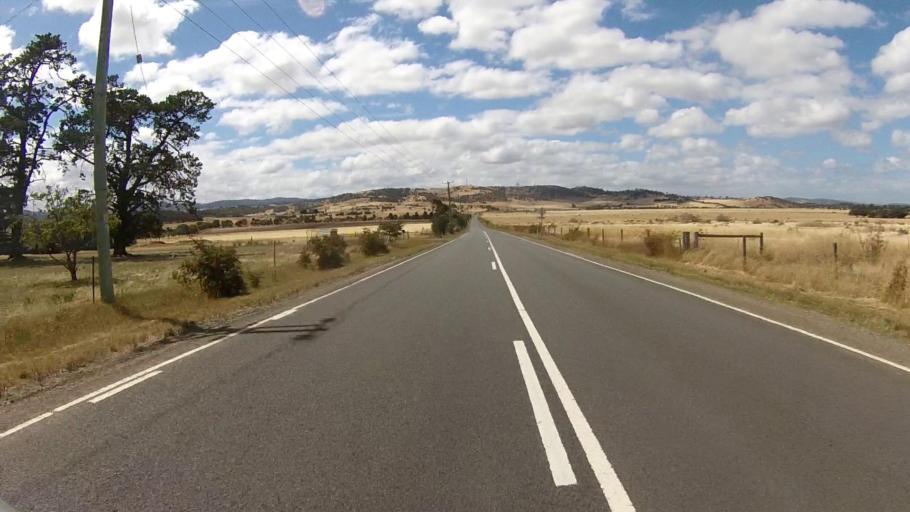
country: AU
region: Tasmania
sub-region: Sorell
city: Sorell
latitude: -42.7594
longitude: 147.5193
